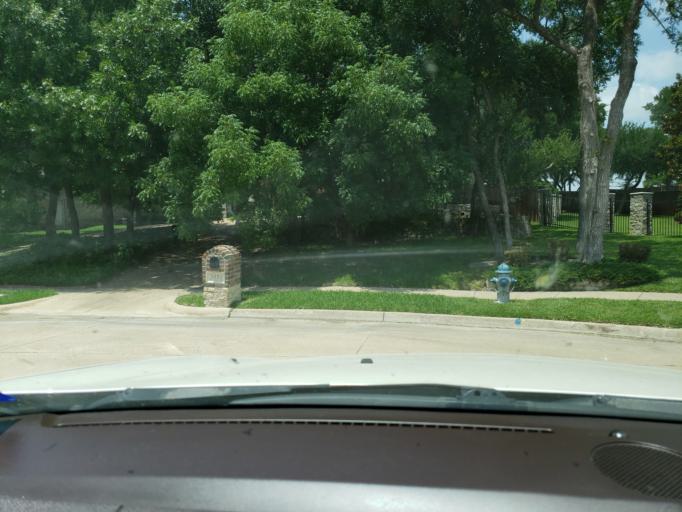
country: US
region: Texas
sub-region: Dallas County
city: Rowlett
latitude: 32.8945
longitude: -96.5545
